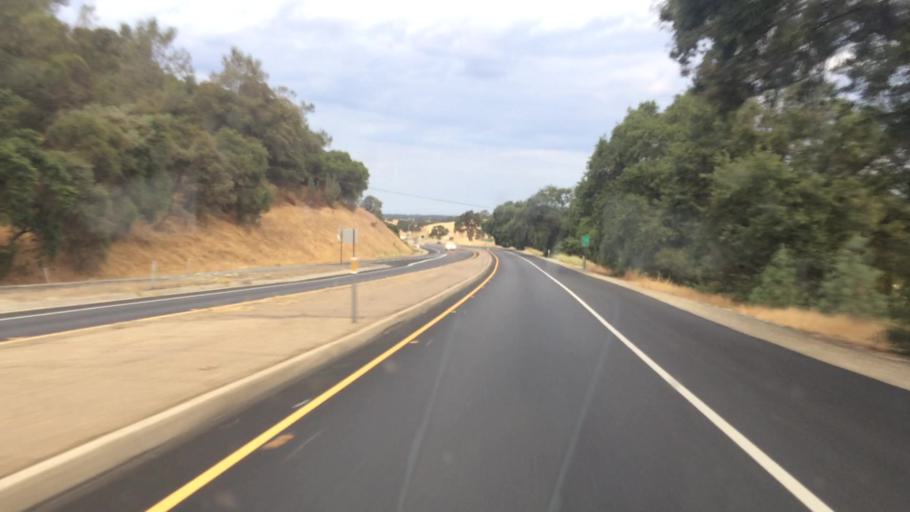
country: US
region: California
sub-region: Amador County
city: Plymouth
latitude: 38.4549
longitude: -120.8684
